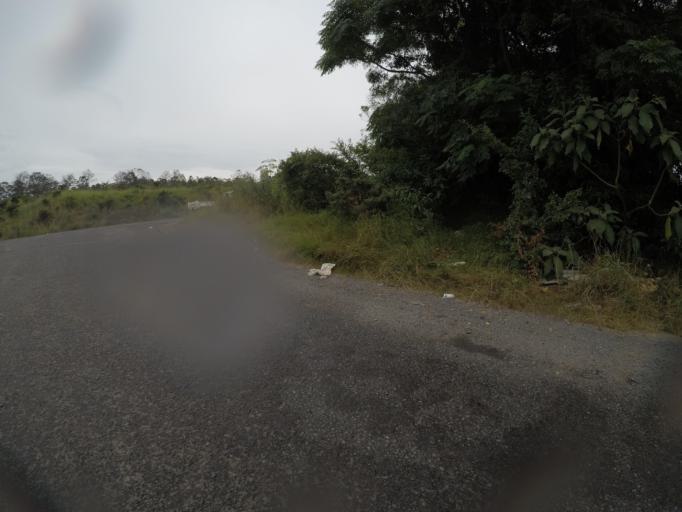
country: ZA
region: Eastern Cape
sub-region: Buffalo City Metropolitan Municipality
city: East London
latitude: -32.9811
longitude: 27.8227
